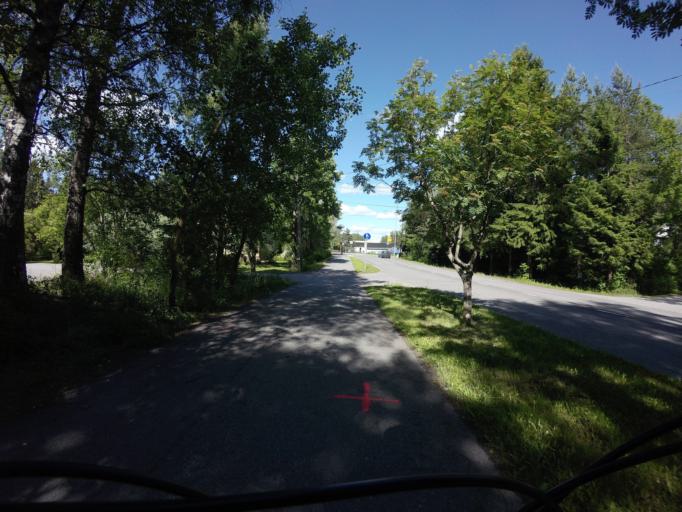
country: FI
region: Varsinais-Suomi
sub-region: Turku
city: Vahto
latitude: 60.5328
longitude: 22.3042
